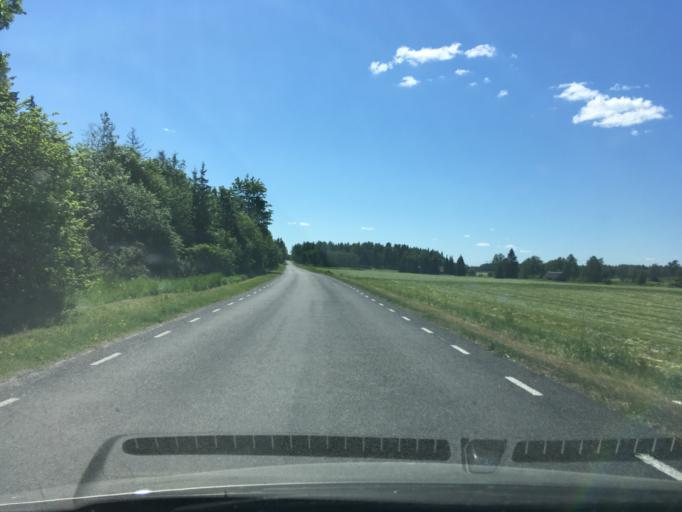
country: EE
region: Raplamaa
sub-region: Kohila vald
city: Kohila
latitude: 59.1362
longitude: 24.8429
